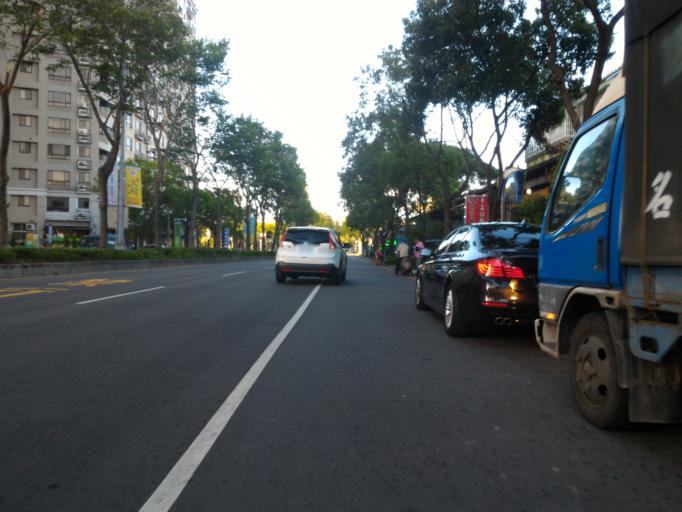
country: TW
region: Taiwan
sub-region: Taoyuan
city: Taoyuan
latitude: 24.9489
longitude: 121.3856
